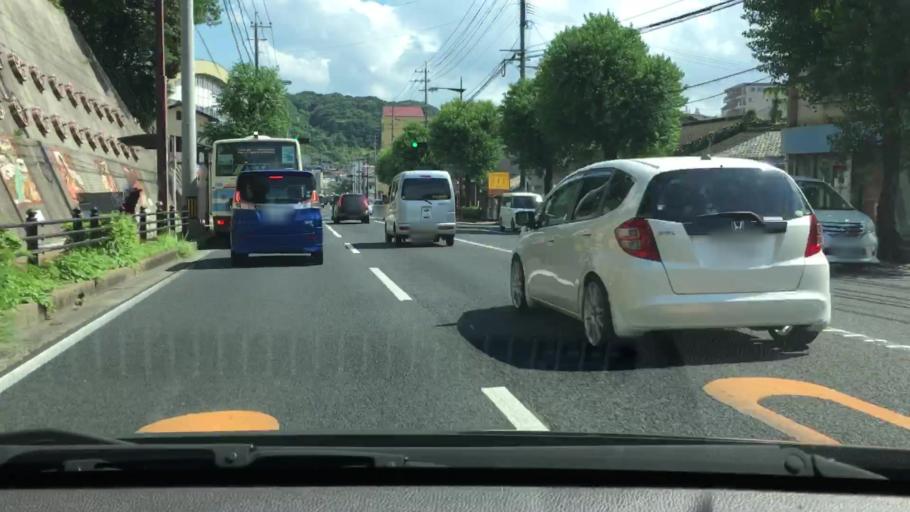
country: JP
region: Nagasaki
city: Sasebo
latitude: 33.2014
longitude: 129.7210
